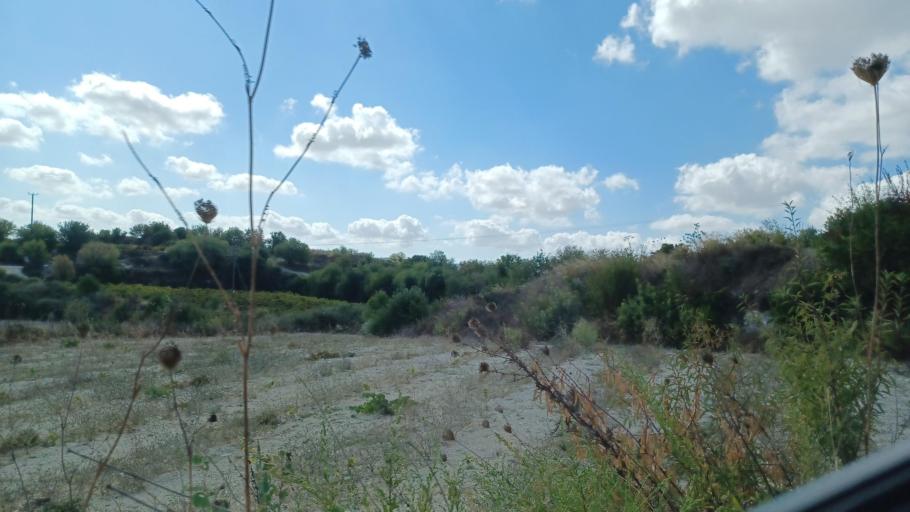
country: CY
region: Pafos
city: Mesogi
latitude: 34.8436
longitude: 32.5365
